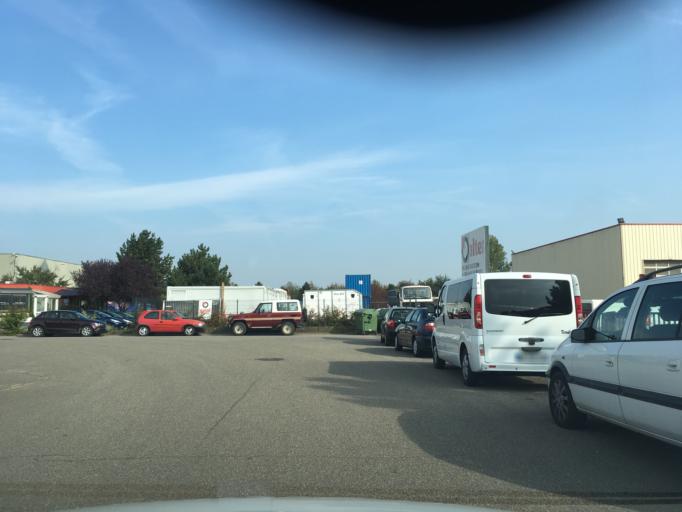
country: FR
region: Alsace
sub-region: Departement du Haut-Rhin
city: Houssen
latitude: 48.1056
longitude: 7.3814
